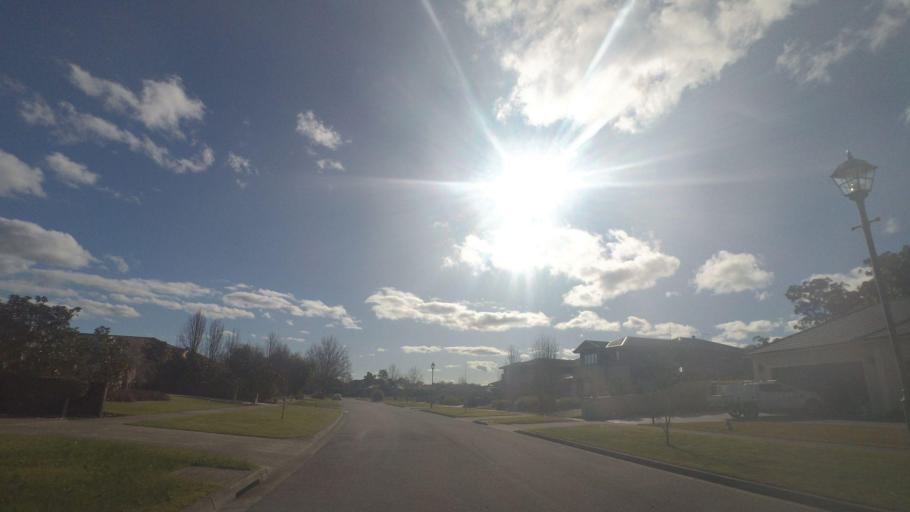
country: AU
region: Victoria
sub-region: Yarra Ranges
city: Lysterfield
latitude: -37.9197
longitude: 145.2904
